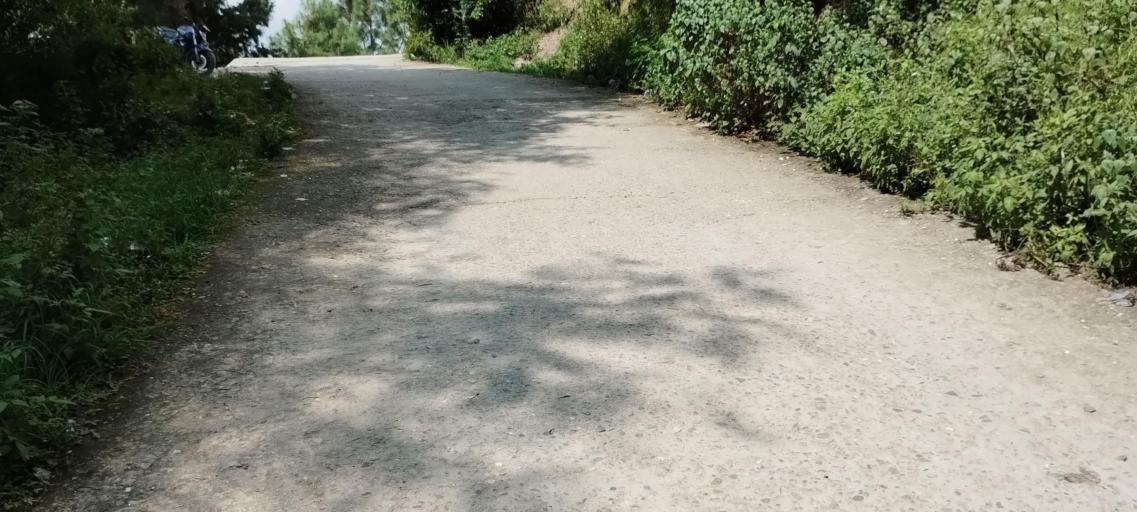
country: NP
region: Central Region
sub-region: Bagmati Zone
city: Kathmandu
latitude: 27.7892
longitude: 85.3612
